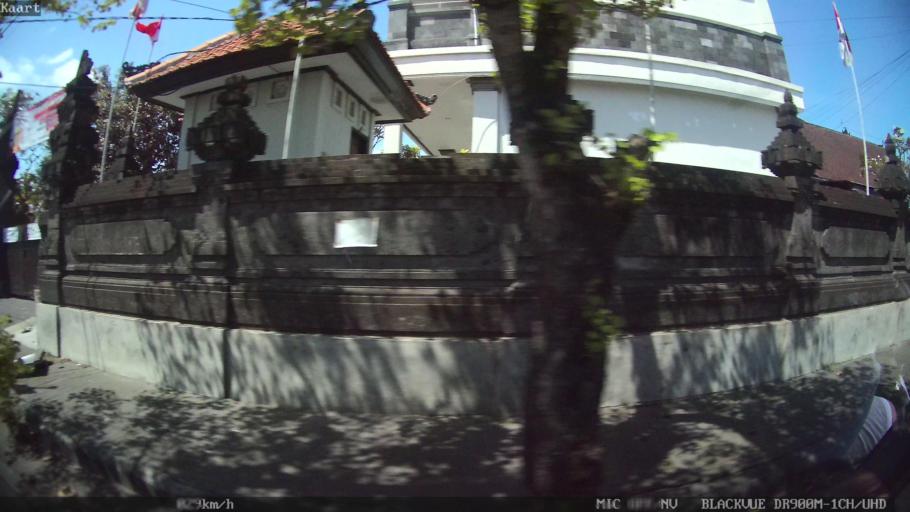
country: ID
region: Bali
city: Banjar Gunungpande
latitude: -8.6561
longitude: 115.1626
